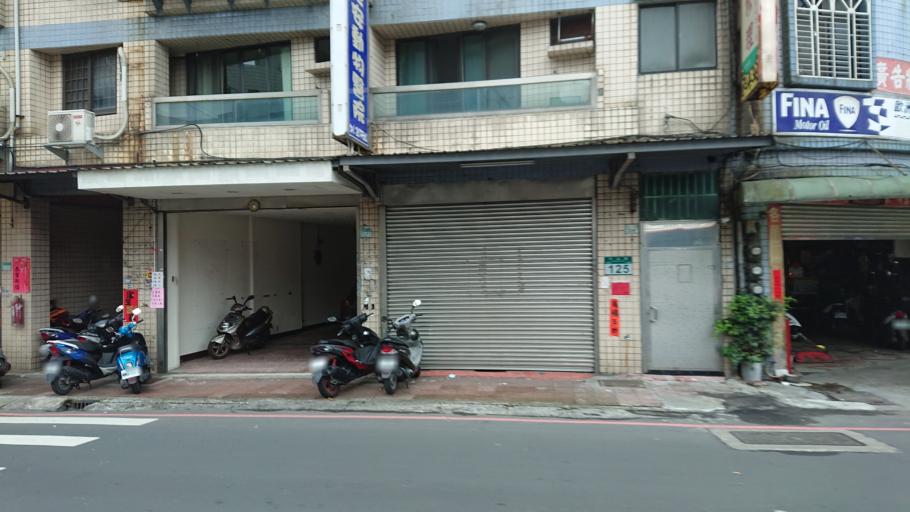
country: TW
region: Taiwan
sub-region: Taoyuan
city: Taoyuan
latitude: 24.9570
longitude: 121.3498
